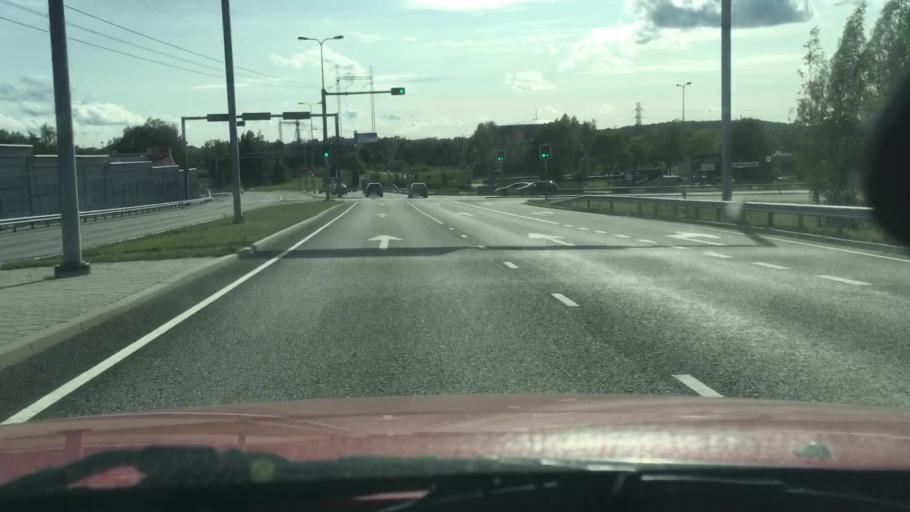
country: FI
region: Varsinais-Suomi
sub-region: Turku
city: Raisio
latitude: 60.4611
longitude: 22.1979
